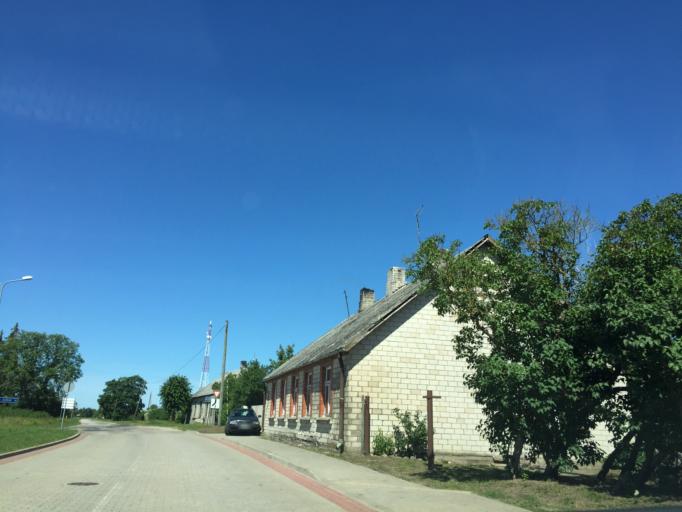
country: LV
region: Ventspils Rajons
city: Piltene
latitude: 57.2302
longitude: 21.6673
